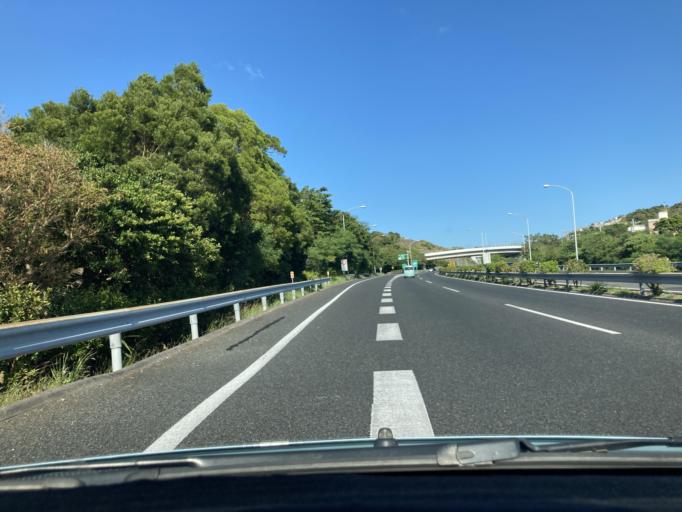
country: JP
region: Okinawa
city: Ginowan
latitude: 26.2465
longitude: 127.7479
